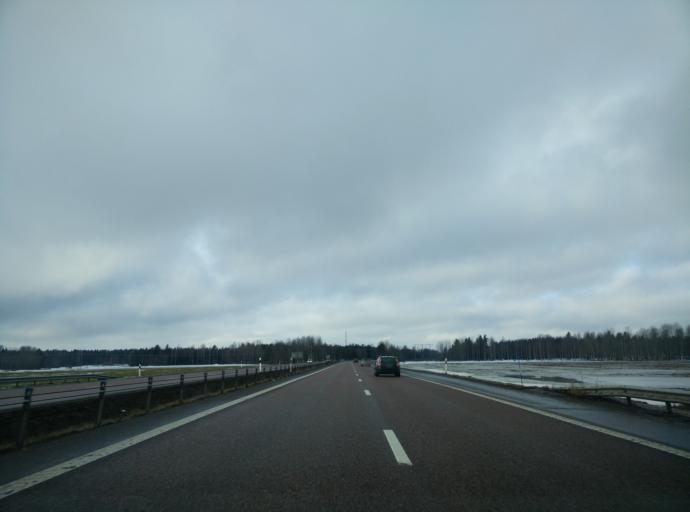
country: SE
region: Gaevleborg
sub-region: Gavle Kommun
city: Valbo
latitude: 60.6289
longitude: 16.9715
